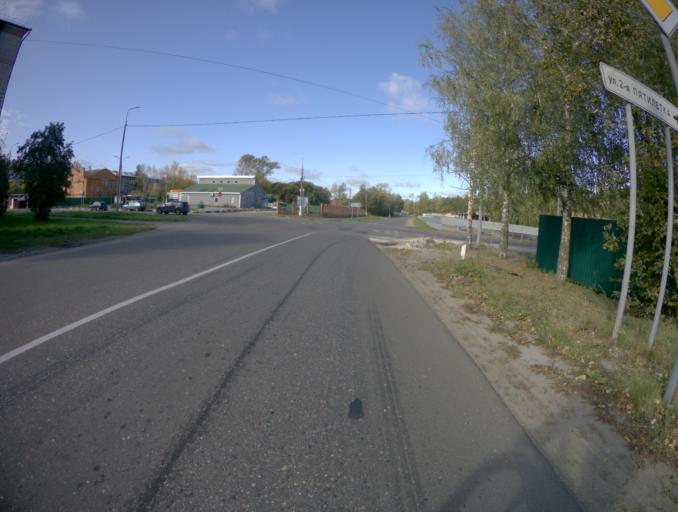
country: RU
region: Moskovskaya
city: Roshal'
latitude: 55.6596
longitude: 39.8876
